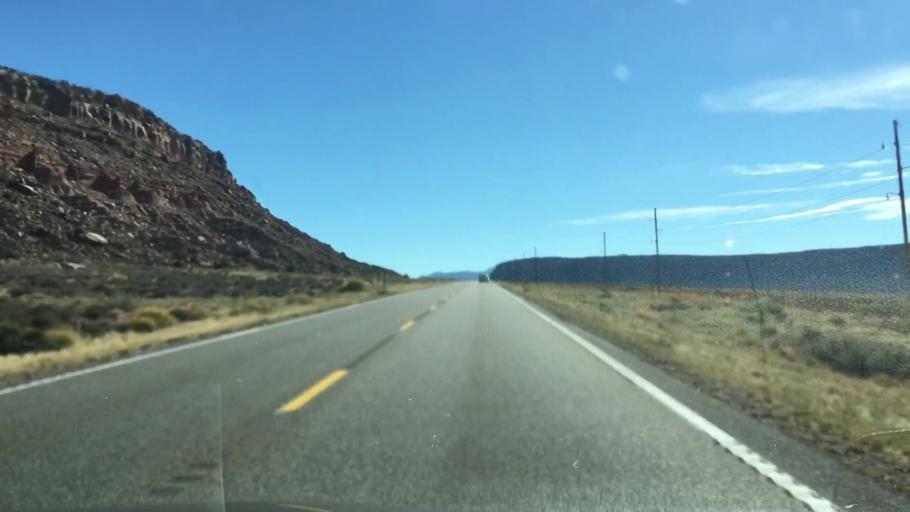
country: US
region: Utah
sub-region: Washington County
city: Hurricane
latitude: 37.1241
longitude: -113.1984
